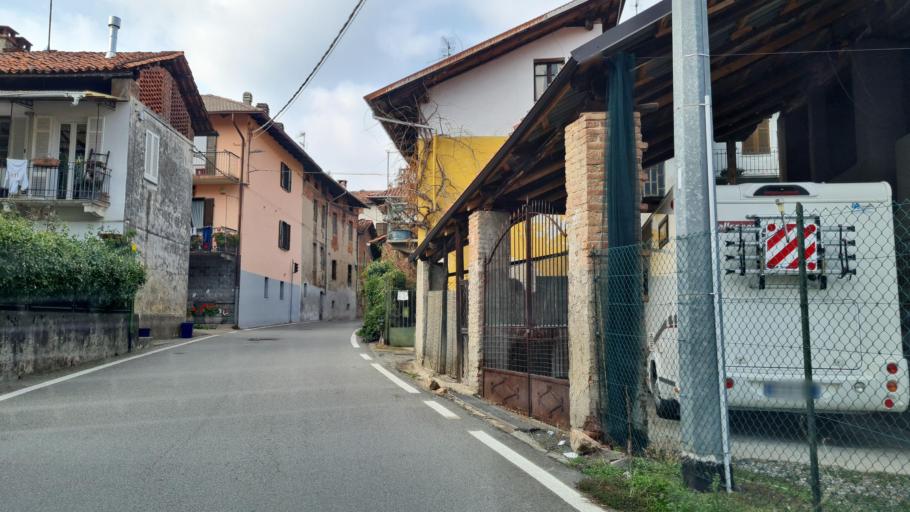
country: IT
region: Piedmont
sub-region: Provincia di Biella
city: Villa
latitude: 45.6003
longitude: 8.1910
